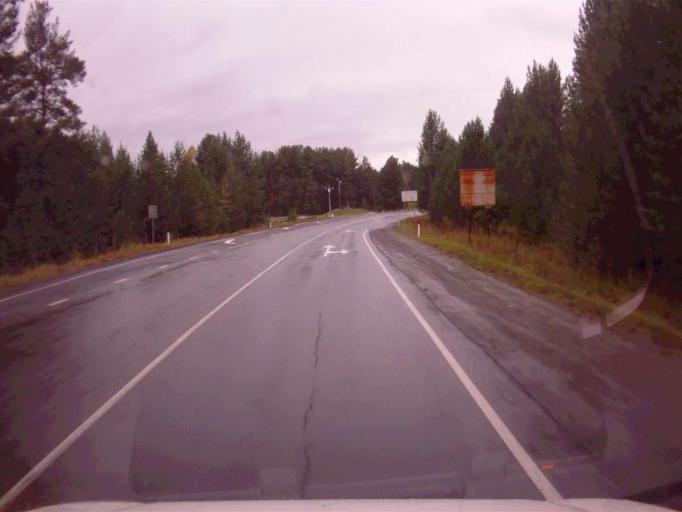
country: RU
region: Chelyabinsk
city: Verkhniy Ufaley
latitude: 56.0276
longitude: 60.2882
